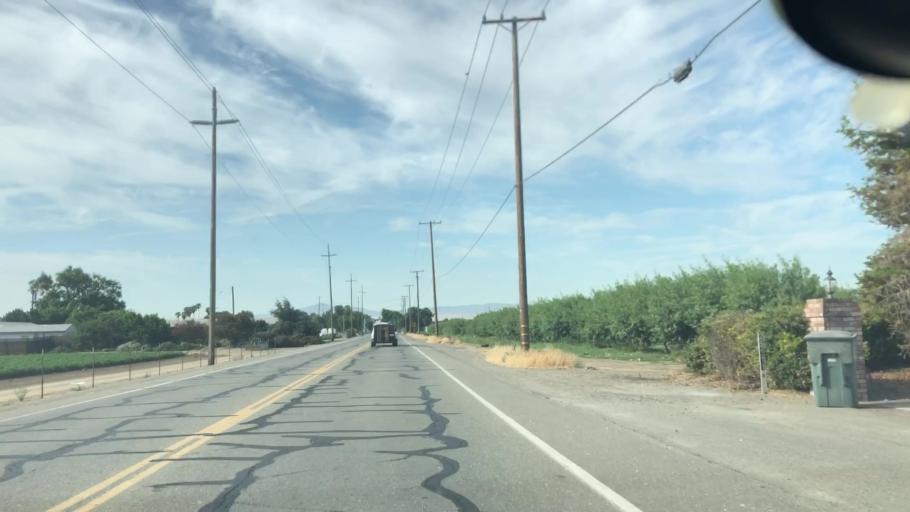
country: US
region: California
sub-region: San Joaquin County
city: Tracy
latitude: 37.7288
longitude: -121.3983
